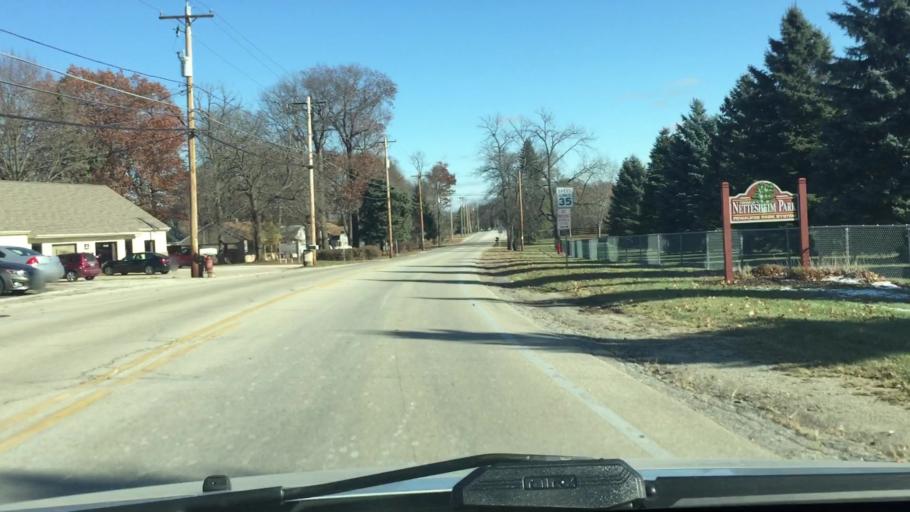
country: US
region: Wisconsin
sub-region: Waukesha County
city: Pewaukee
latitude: 43.0668
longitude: -88.2948
